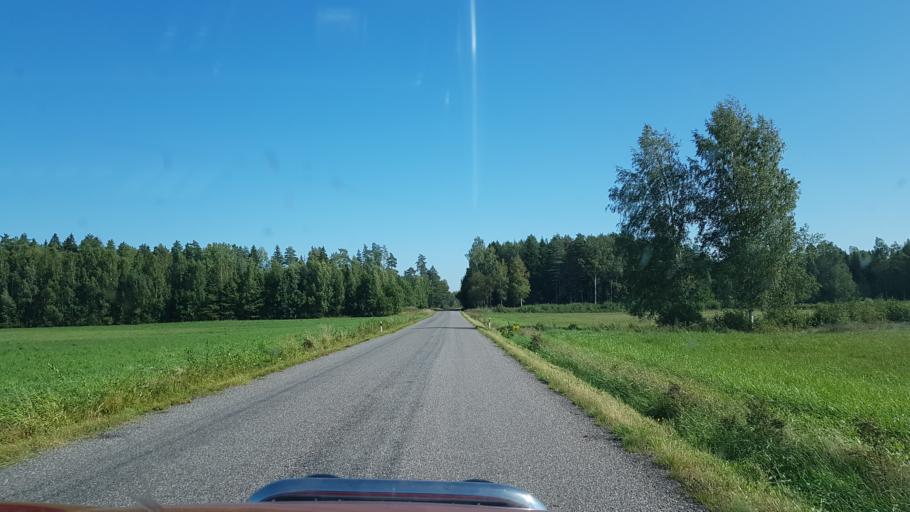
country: EE
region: Polvamaa
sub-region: Polva linn
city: Polva
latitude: 58.2092
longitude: 27.0827
